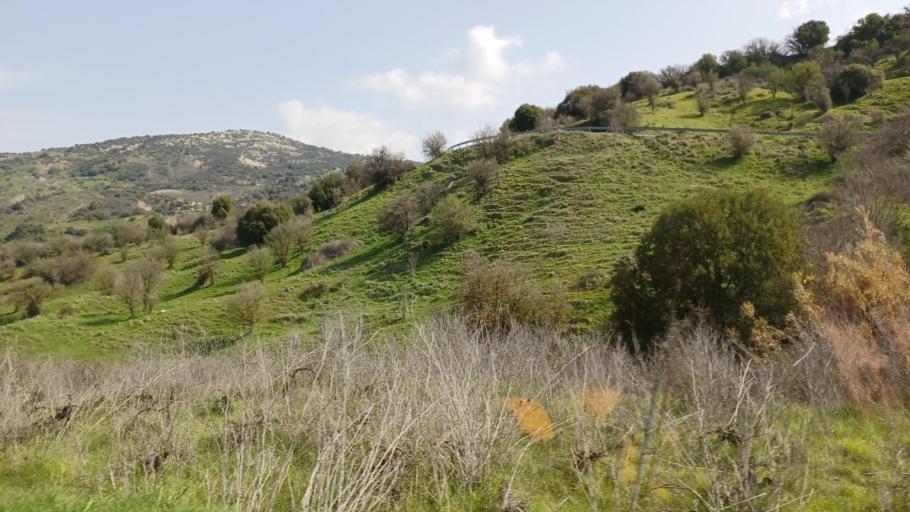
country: CY
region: Limassol
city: Pissouri
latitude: 34.7573
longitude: 32.6474
